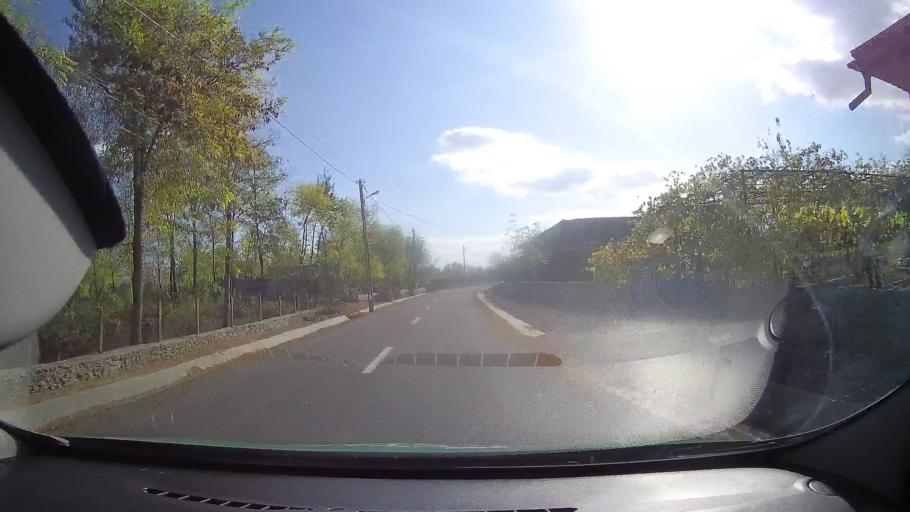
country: RO
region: Constanta
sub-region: Comuna Istria
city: Istria
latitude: 44.5751
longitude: 28.7135
